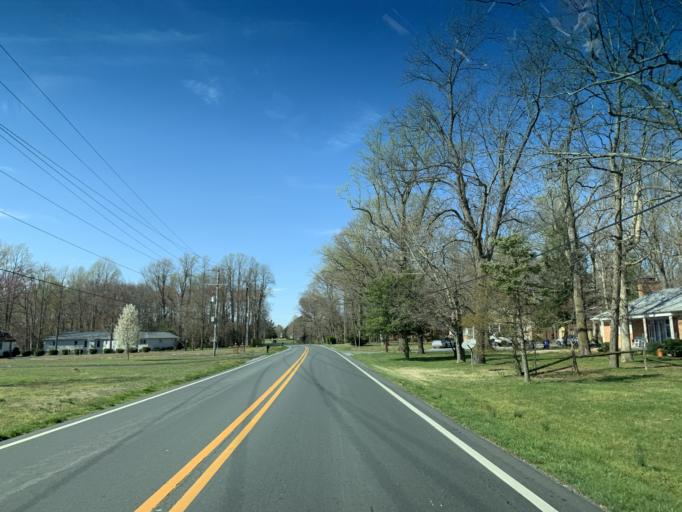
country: US
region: Delaware
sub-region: Sussex County
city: Milford
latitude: 38.9347
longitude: -75.4579
